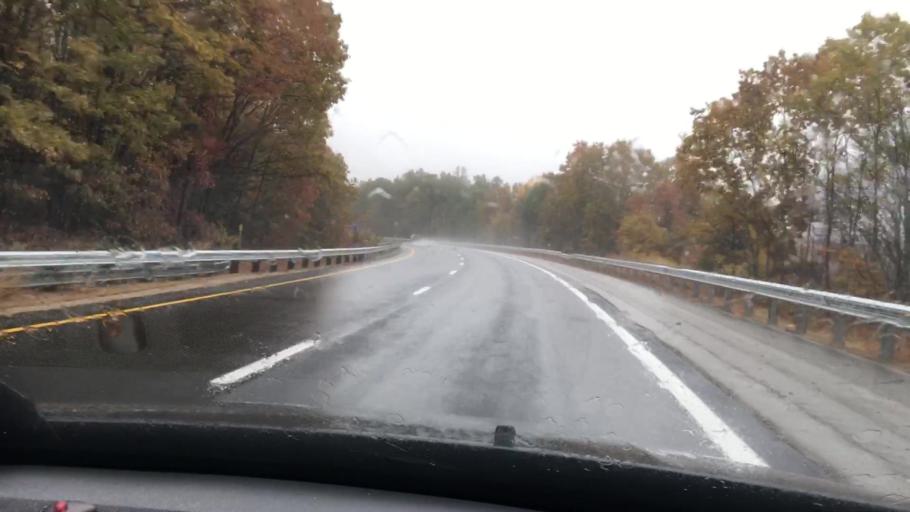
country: US
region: New Hampshire
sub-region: Merrimack County
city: Boscawen
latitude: 43.3388
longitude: -71.6159
